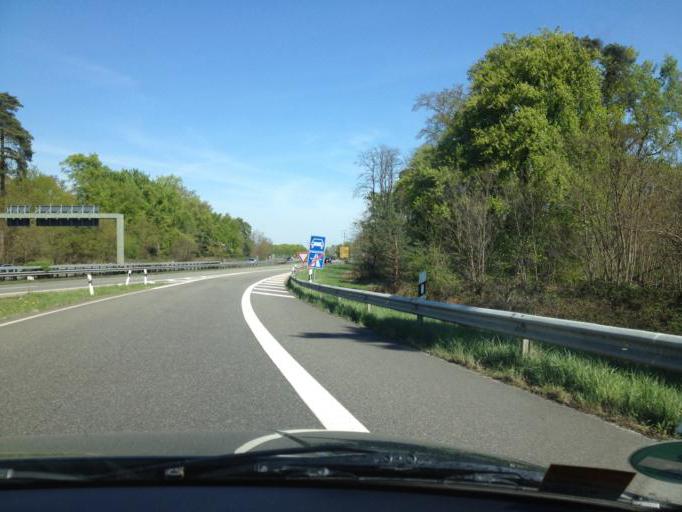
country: DE
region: Rheinland-Pfalz
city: Otterstadt
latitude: 49.3556
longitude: 8.4239
